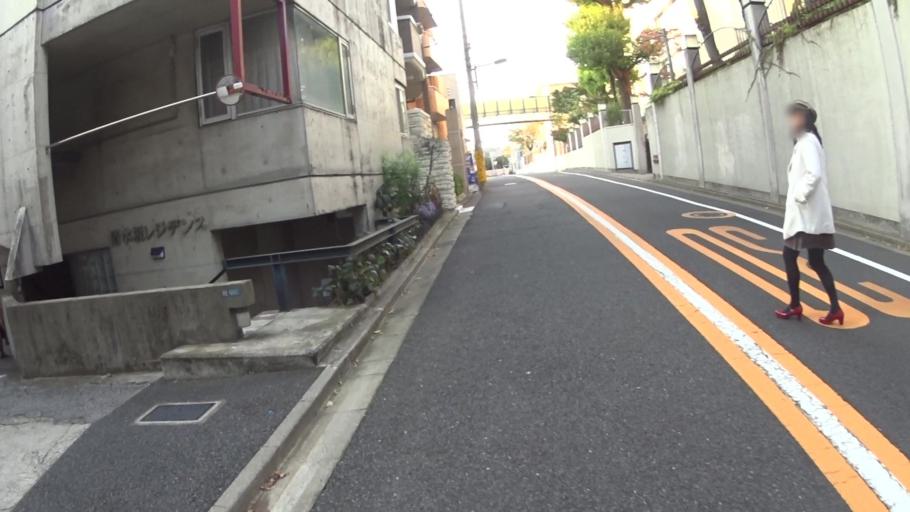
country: JP
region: Tokyo
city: Tokyo
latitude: 35.7193
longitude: 139.7686
